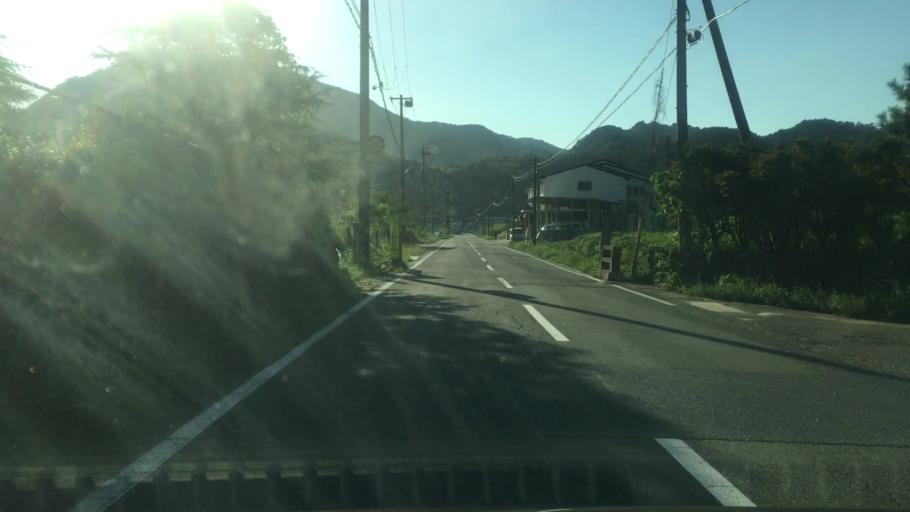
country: JP
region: Hyogo
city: Toyooka
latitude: 35.6190
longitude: 134.8190
